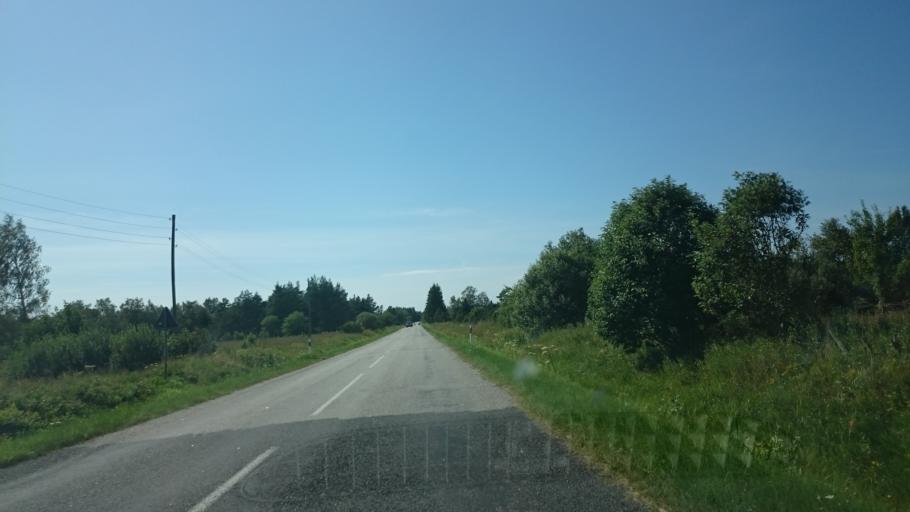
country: EE
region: Saare
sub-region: Orissaare vald
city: Orissaare
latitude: 58.5693
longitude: 22.7581
